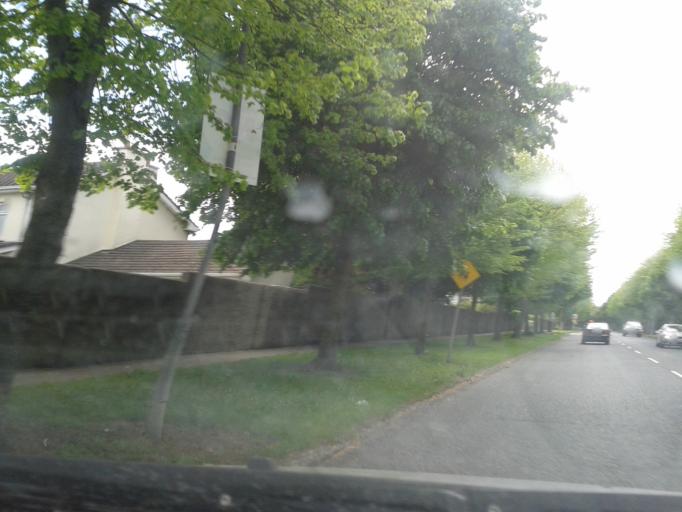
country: IE
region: Leinster
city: Castleknock
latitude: 53.3741
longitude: -6.3585
